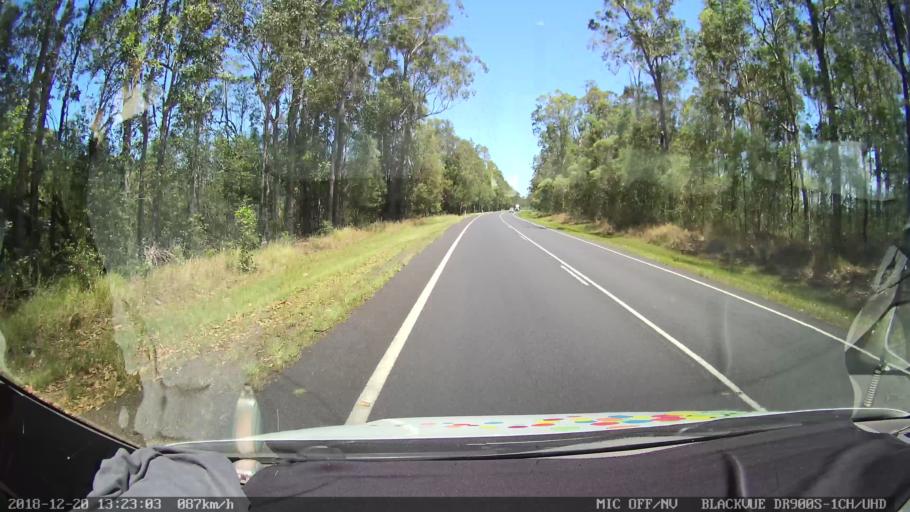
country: AU
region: New South Wales
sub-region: Richmond Valley
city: Casino
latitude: -29.0994
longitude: 153.0009
